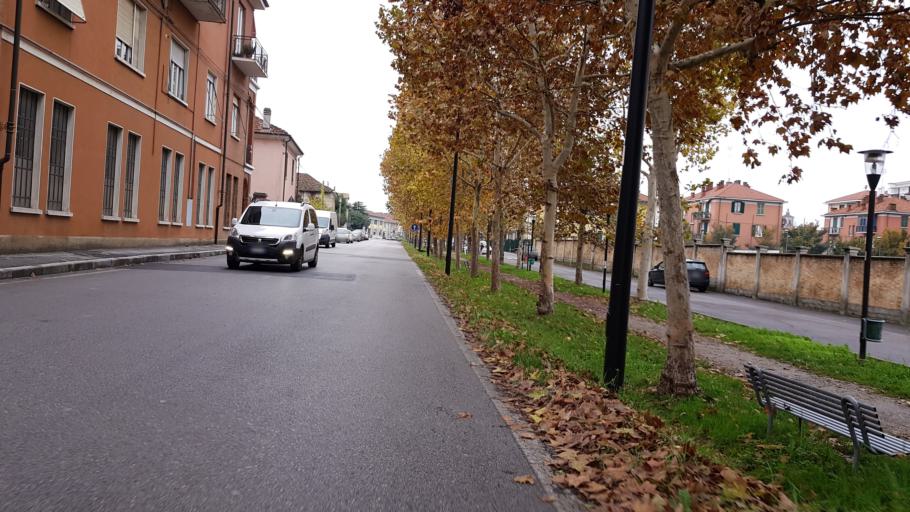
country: IT
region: Piedmont
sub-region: Provincia di Cuneo
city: Fossano
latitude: 44.5541
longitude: 7.7305
